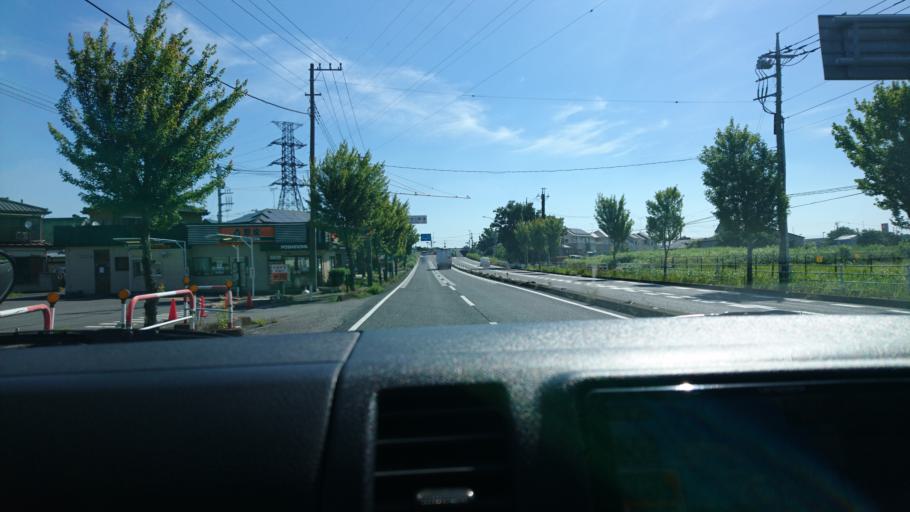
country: JP
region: Saitama
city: Kurihashi
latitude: 36.1318
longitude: 139.7047
